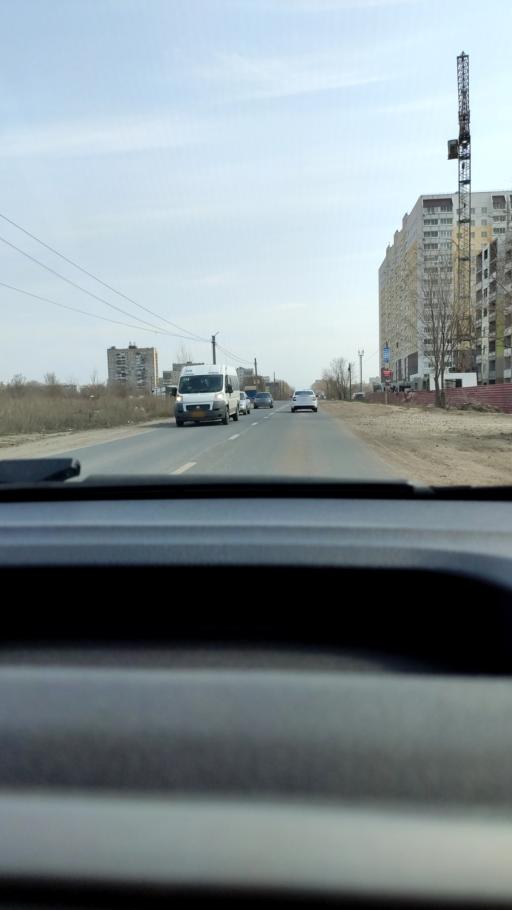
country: RU
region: Samara
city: Tol'yatti
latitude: 53.5095
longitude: 49.2481
